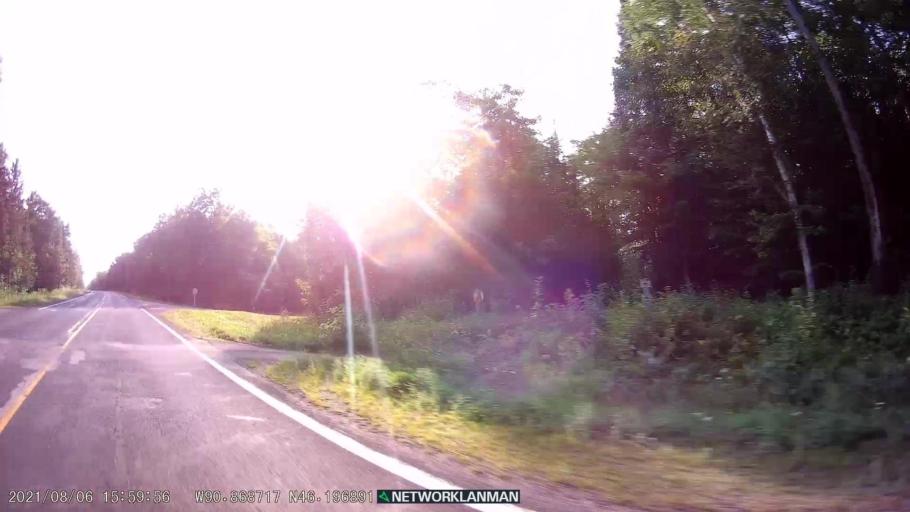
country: US
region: Wisconsin
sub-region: Ashland County
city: Ashland
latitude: 46.1971
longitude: -90.8687
